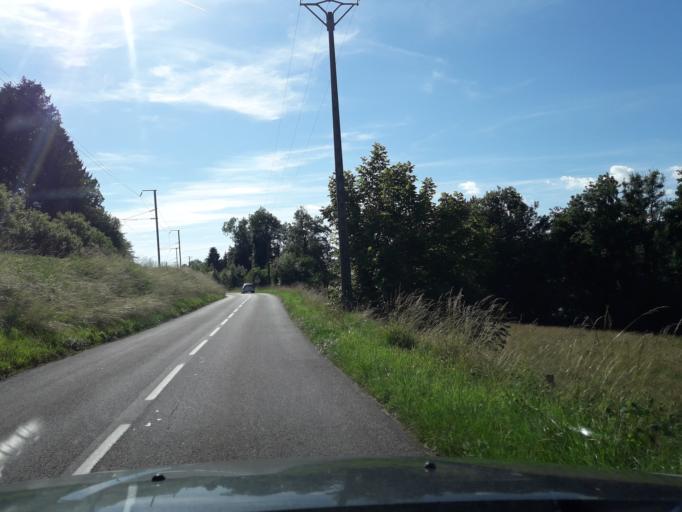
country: FR
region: Rhone-Alpes
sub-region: Departement de la Savoie
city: La Bridoire
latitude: 45.5392
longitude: 5.7874
